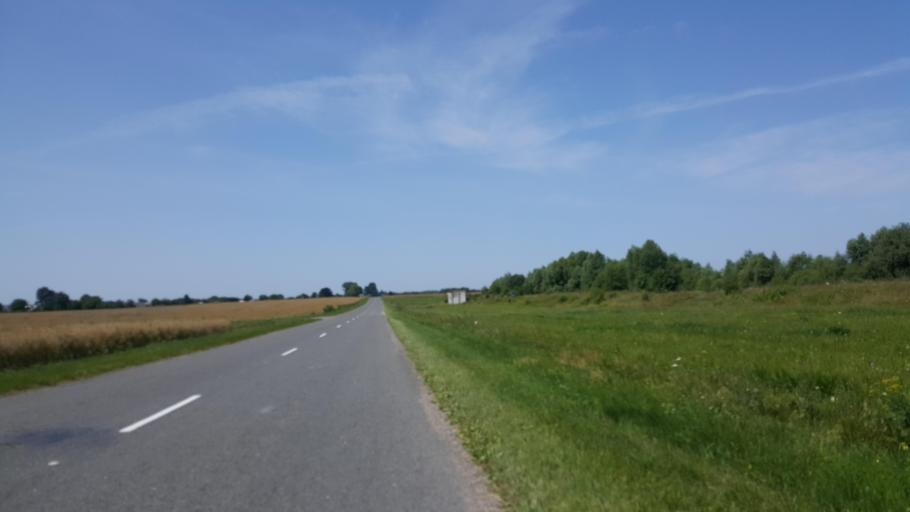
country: BY
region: Brest
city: Vysokaye
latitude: 52.3675
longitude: 23.5349
